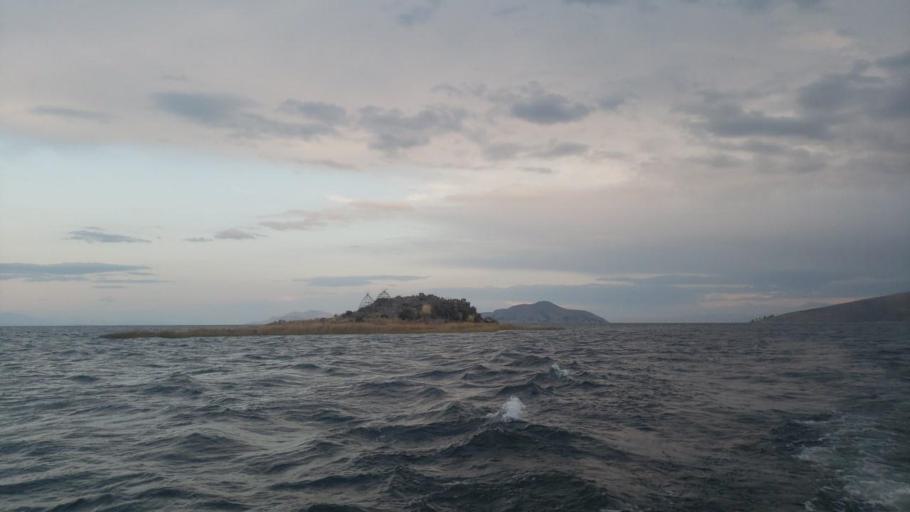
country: BO
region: La Paz
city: San Pedro
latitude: -16.2389
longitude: -68.8285
